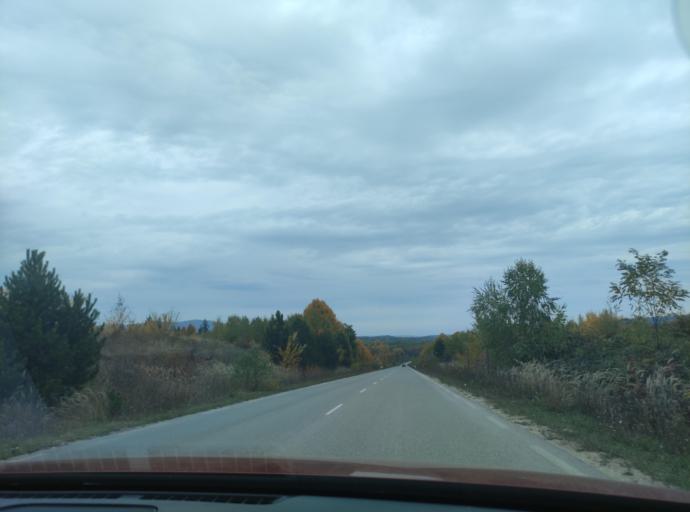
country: BG
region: Montana
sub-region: Obshtina Berkovitsa
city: Berkovitsa
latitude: 43.2284
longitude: 23.1576
